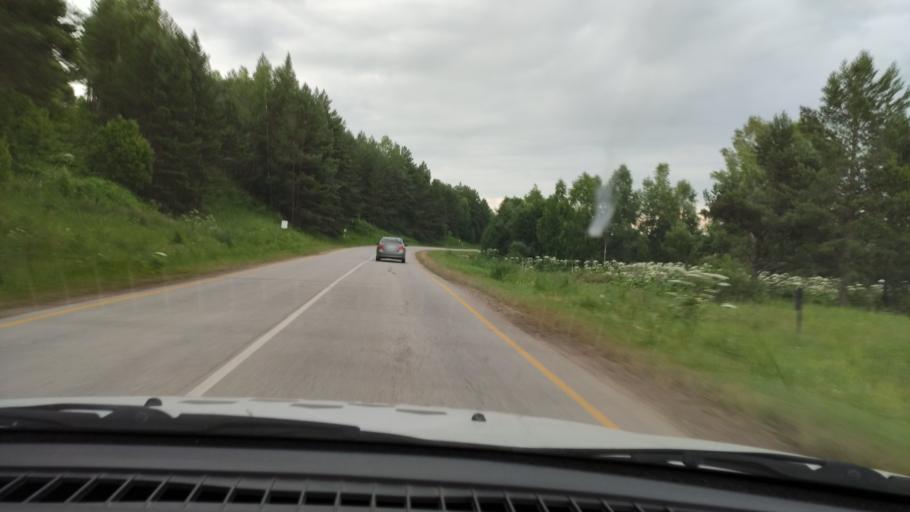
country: RU
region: Perm
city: Kukushtan
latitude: 57.4905
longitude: 56.6335
